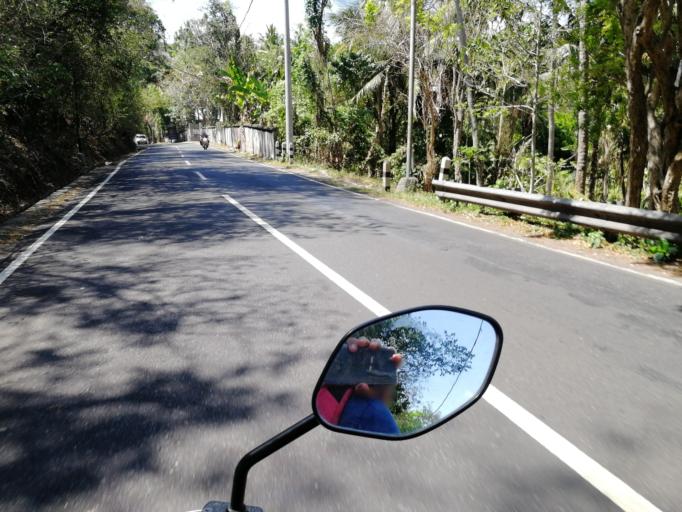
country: ID
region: Bali
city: Padangbai
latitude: -8.5271
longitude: 115.5042
